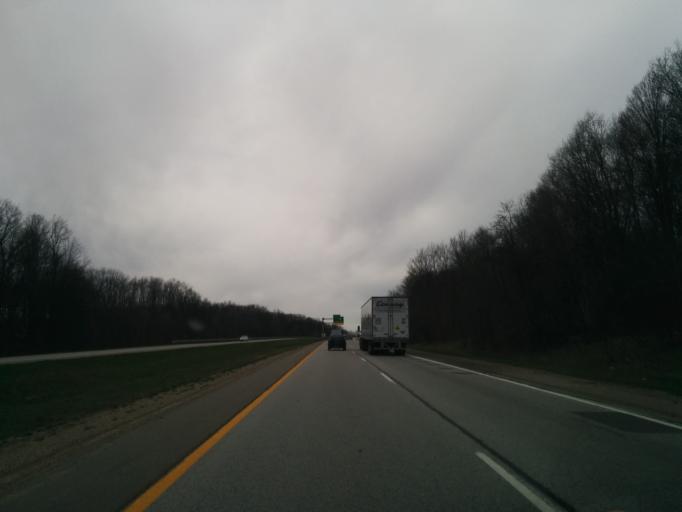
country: US
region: Michigan
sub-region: Ottawa County
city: Jenison
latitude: 42.8727
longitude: -85.7891
